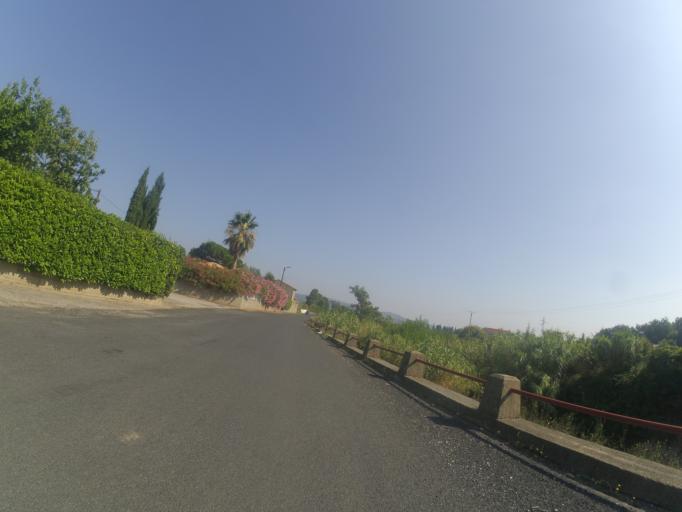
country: FR
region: Languedoc-Roussillon
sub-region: Departement des Pyrenees-Orientales
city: Ille-sur-Tet
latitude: 42.6522
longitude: 2.6234
